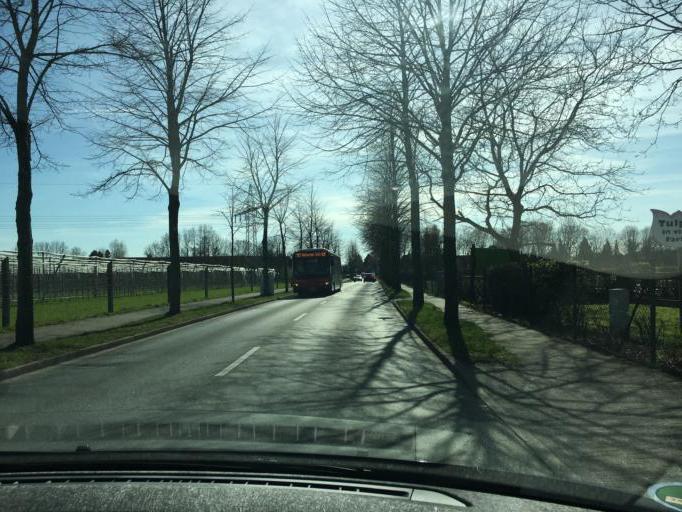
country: DE
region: North Rhine-Westphalia
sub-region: Regierungsbezirk Dusseldorf
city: Ratingen
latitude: 51.3051
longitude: 6.8152
